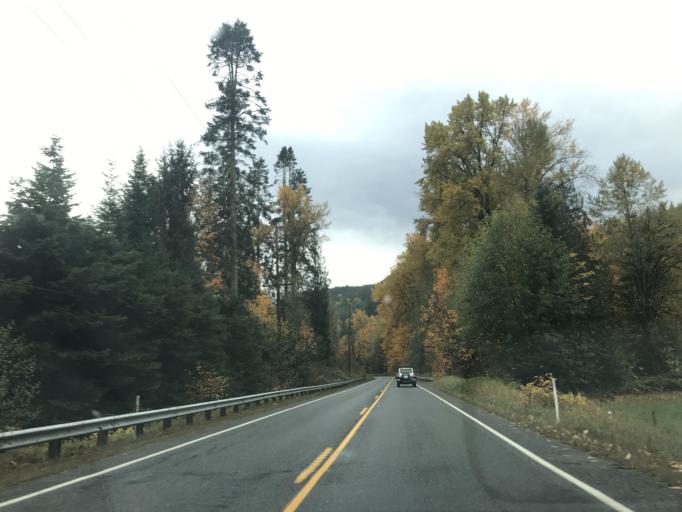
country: US
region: Washington
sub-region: Whatcom County
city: Peaceful Valley
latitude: 48.8827
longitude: -122.1558
